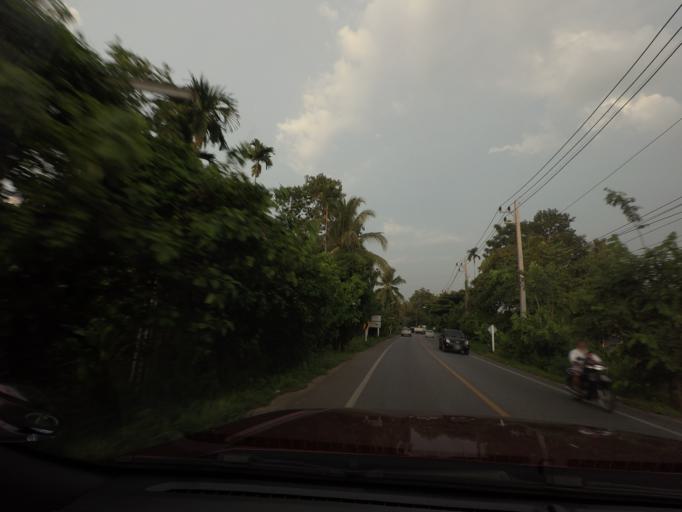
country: TH
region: Yala
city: Yala
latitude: 6.5479
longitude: 101.2513
